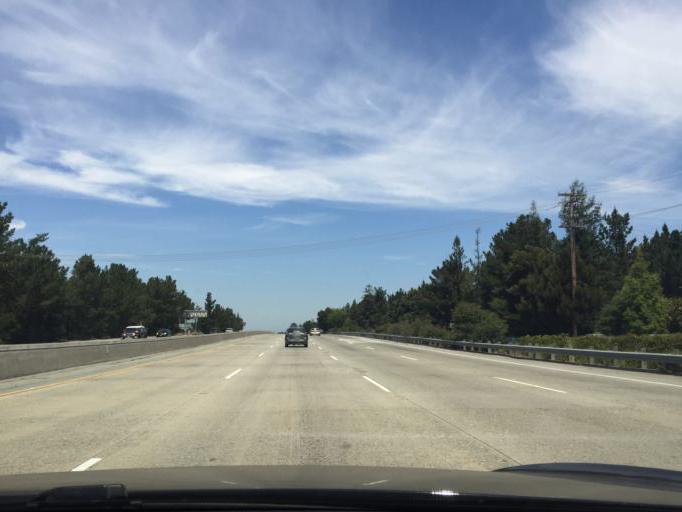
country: US
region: California
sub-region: San Mateo County
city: Hillsborough
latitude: 37.5548
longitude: -122.3787
